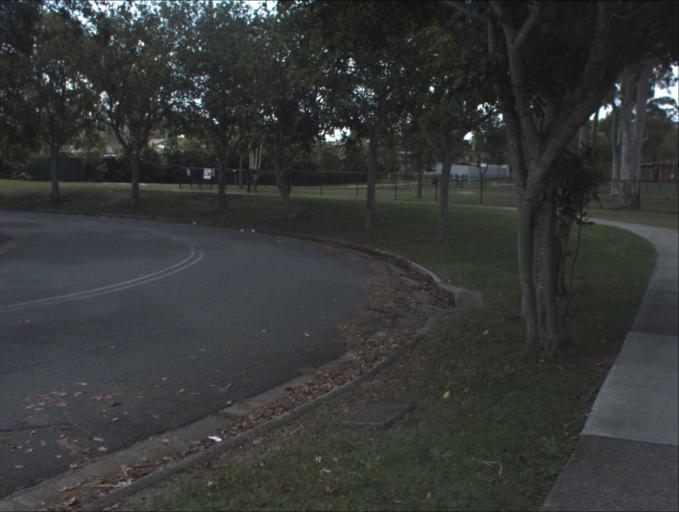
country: AU
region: Queensland
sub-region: Logan
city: Woodridge
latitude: -27.6630
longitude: 153.0576
